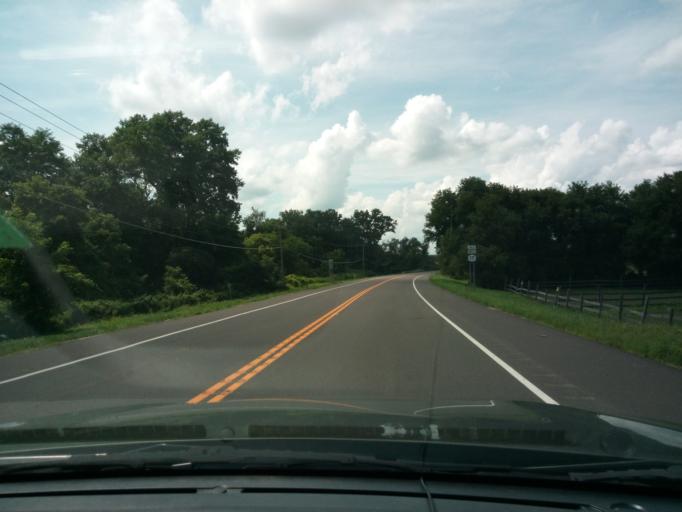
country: US
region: New York
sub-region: Chemung County
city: Southport
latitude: 42.0506
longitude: -76.7771
